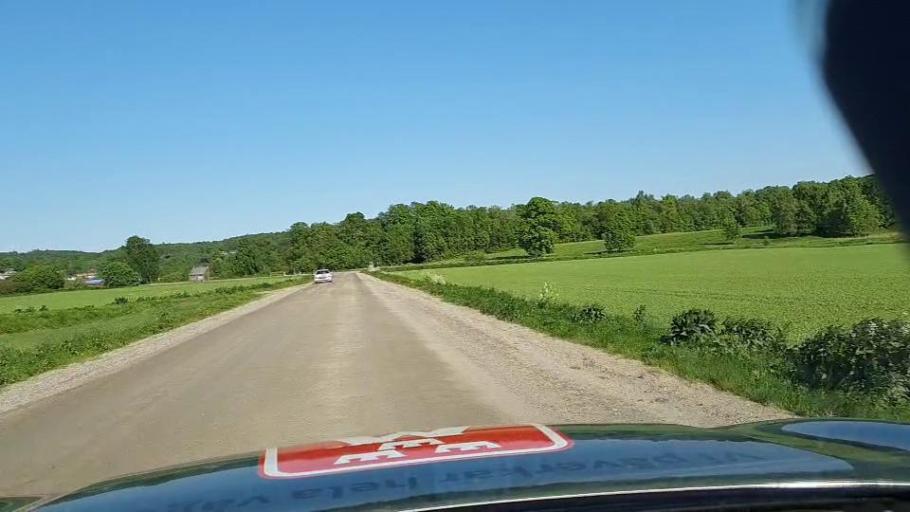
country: SE
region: Skane
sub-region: Hassleholms Kommun
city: Tormestorp
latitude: 56.1128
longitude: 13.7250
